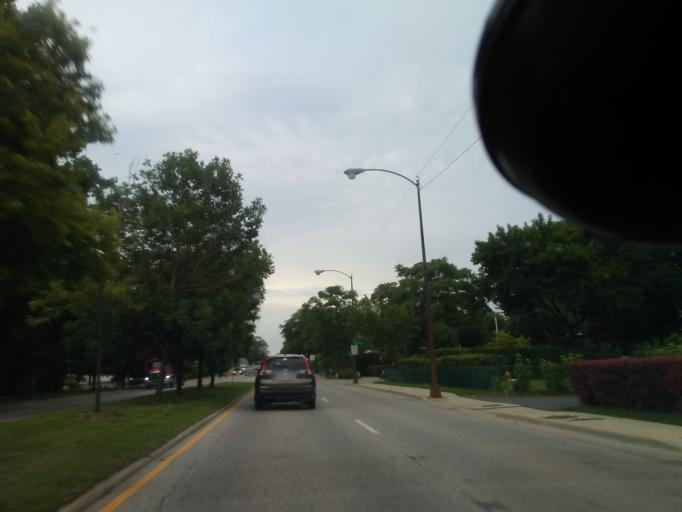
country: US
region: Illinois
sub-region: Cook County
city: Lincolnwood
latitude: 41.9972
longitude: -87.7531
